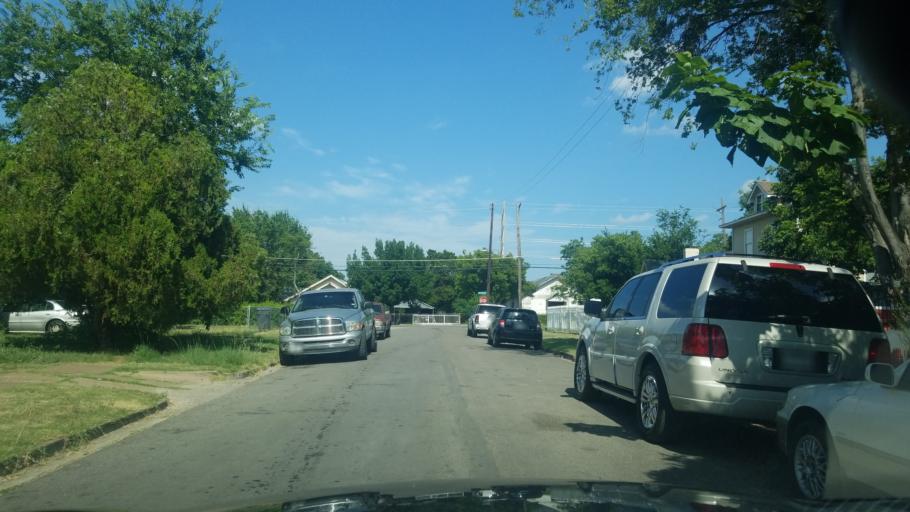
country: US
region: Texas
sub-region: Dallas County
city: Dallas
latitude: 32.7260
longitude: -96.8063
